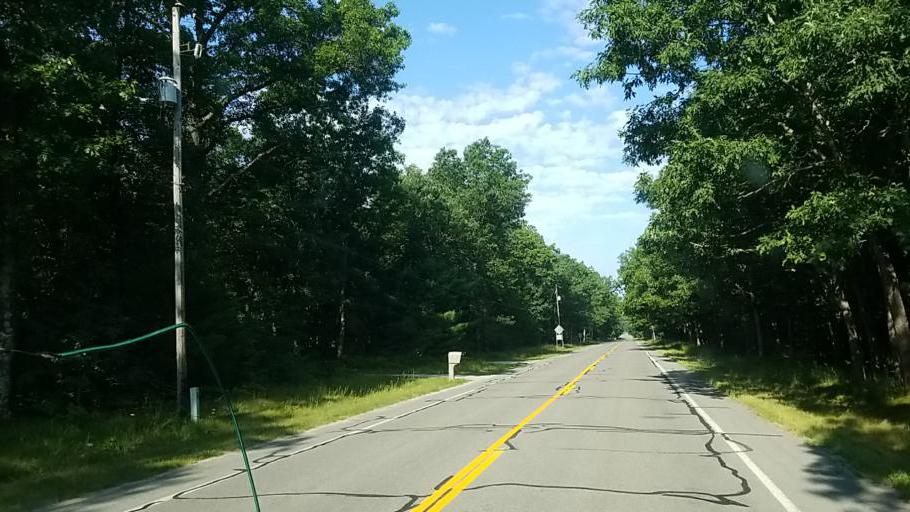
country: US
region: Michigan
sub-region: Muskegon County
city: Lakewood Club
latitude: 43.4695
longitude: -86.2428
